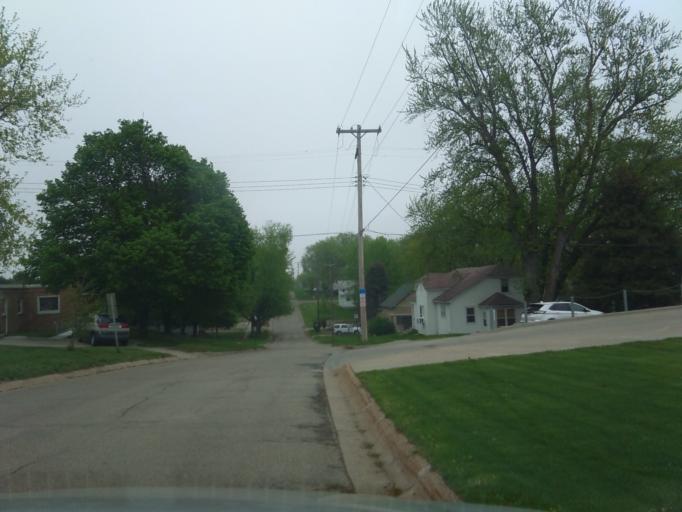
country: US
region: Nebraska
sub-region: Burt County
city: Oakland
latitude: 41.8357
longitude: -96.4631
